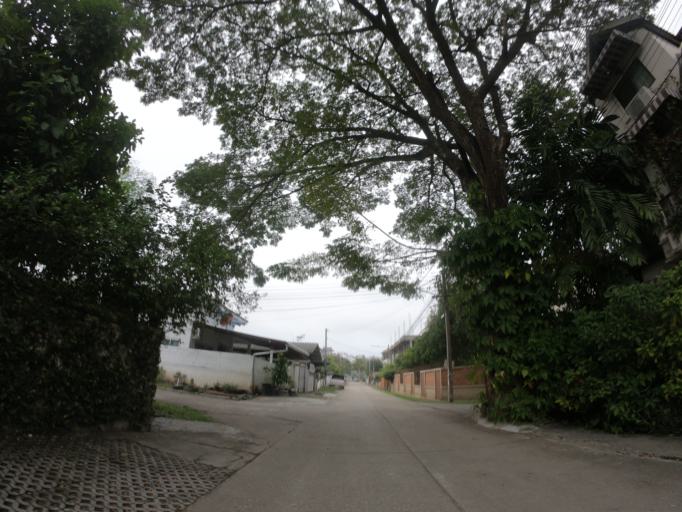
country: TH
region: Chiang Mai
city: Chiang Mai
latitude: 18.7649
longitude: 98.9785
